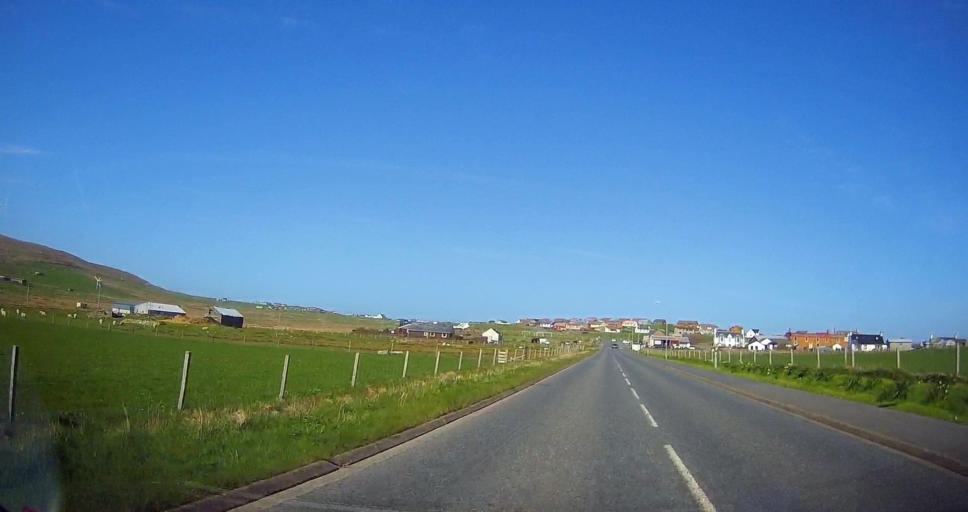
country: GB
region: Scotland
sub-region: Shetland Islands
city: Sandwick
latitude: 60.0016
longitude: -1.2396
